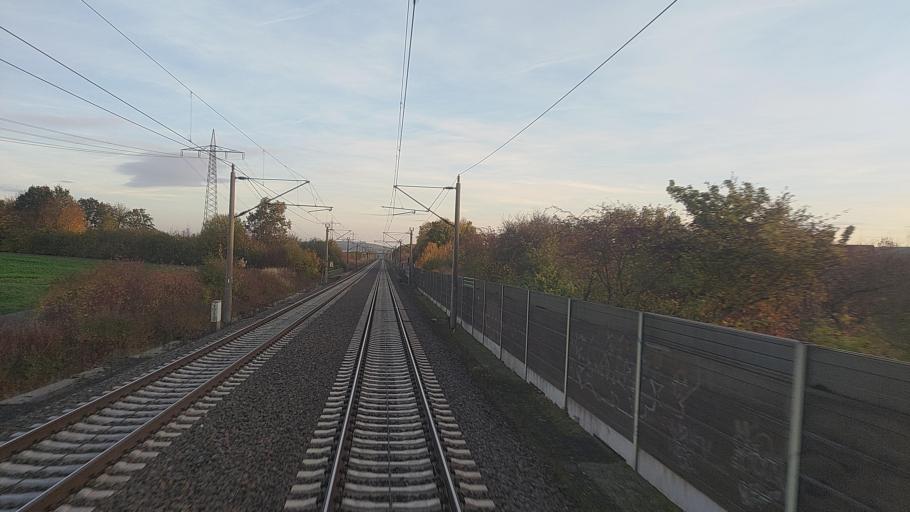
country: DE
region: Lower Saxony
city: Westfeld
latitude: 52.0593
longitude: 9.9135
